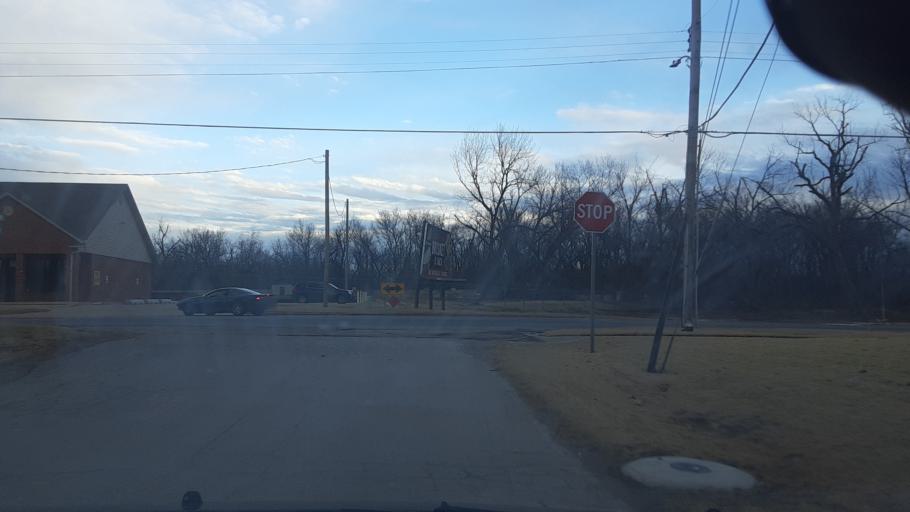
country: US
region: Oklahoma
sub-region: Logan County
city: Guthrie
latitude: 35.8718
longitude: -97.4257
